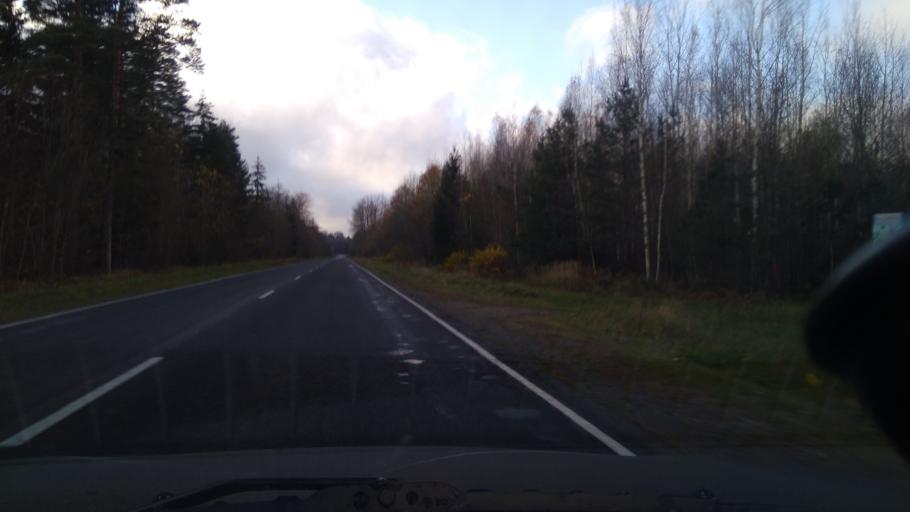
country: BY
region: Minsk
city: Urechcha
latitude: 53.2081
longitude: 27.9285
